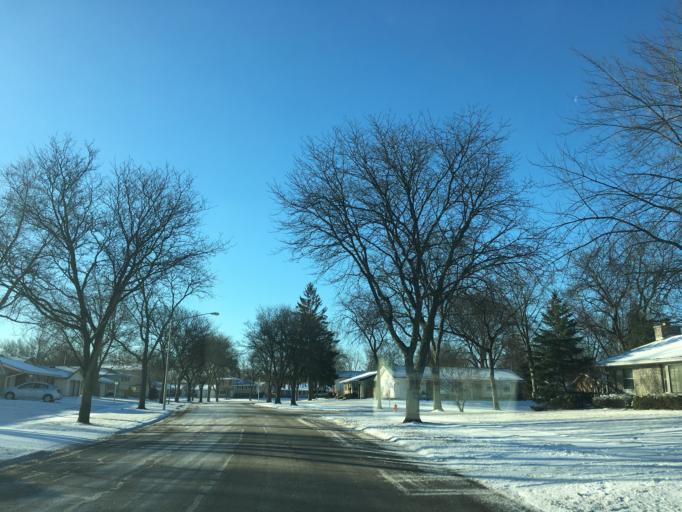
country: US
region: Illinois
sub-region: Cook County
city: Schaumburg
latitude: 42.0192
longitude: -88.1025
